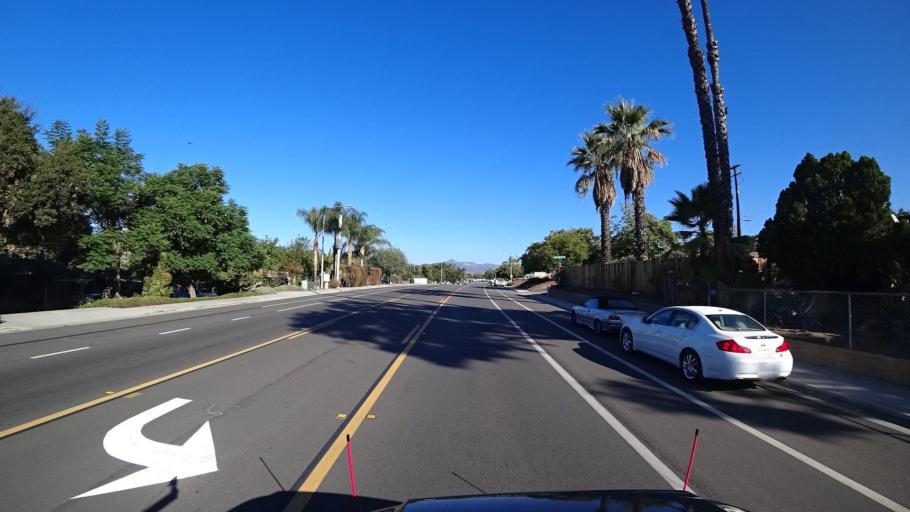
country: US
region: California
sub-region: San Diego County
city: Lakeside
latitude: 32.8518
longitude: -116.9185
